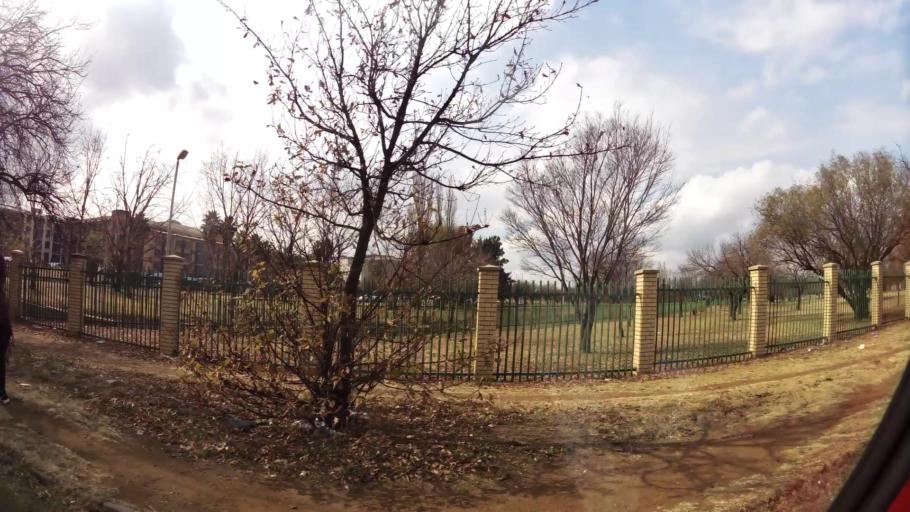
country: ZA
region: Gauteng
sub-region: Sedibeng District Municipality
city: Vanderbijlpark
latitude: -26.7132
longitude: 27.8619
